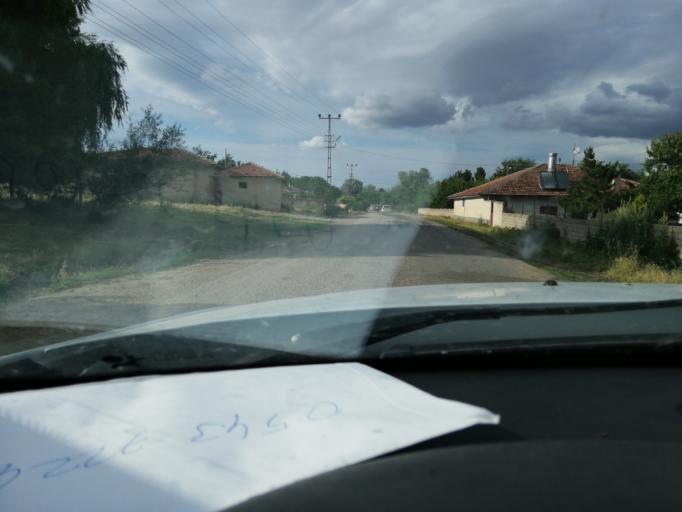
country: TR
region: Kirsehir
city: Kirsehir
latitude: 39.0237
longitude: 34.1245
